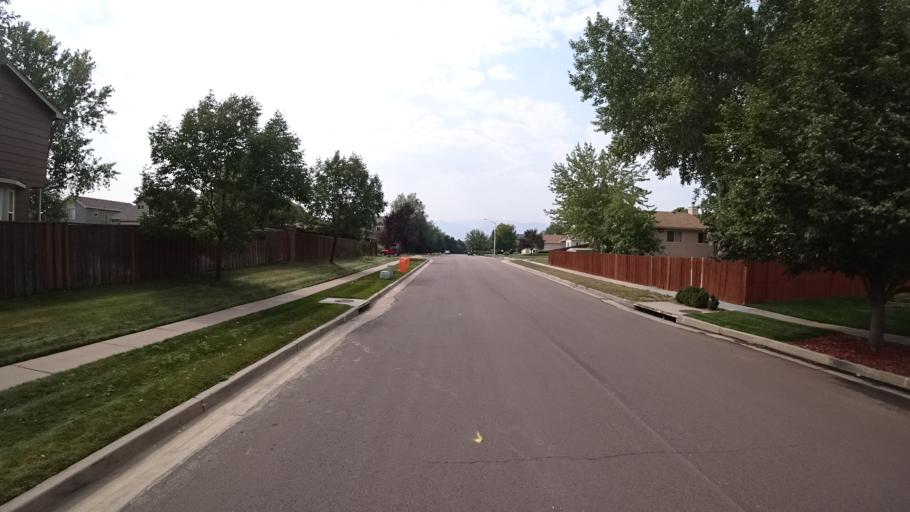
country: US
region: Colorado
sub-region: El Paso County
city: Cimarron Hills
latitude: 38.8222
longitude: -104.7368
